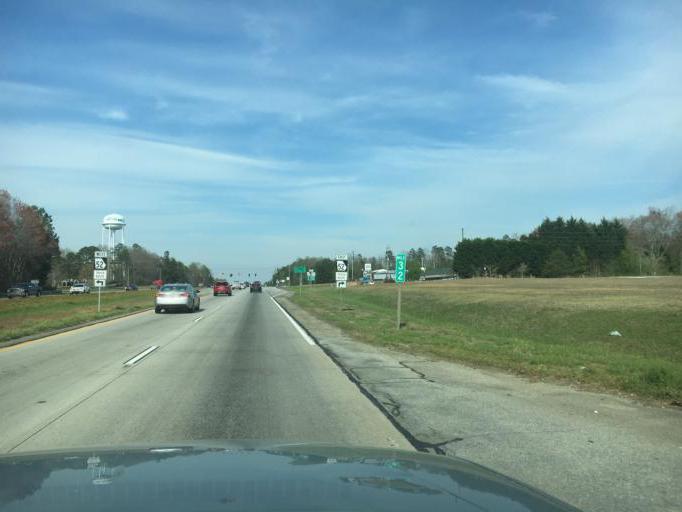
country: US
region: Georgia
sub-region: Hall County
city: Lula
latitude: 34.3933
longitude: -83.6938
